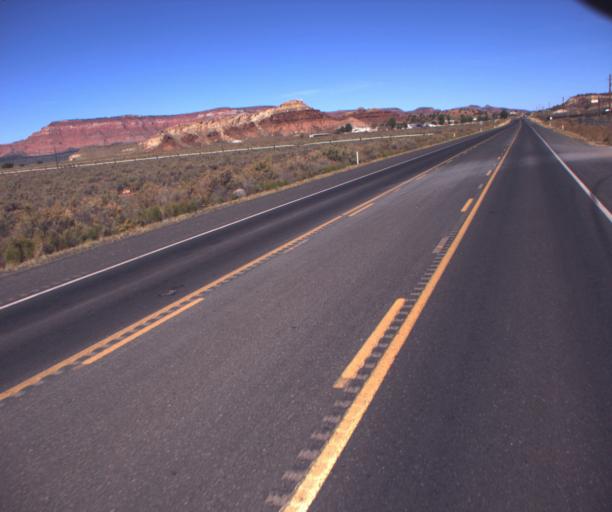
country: US
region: Arizona
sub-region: Coconino County
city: Fredonia
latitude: 36.9729
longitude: -112.5278
